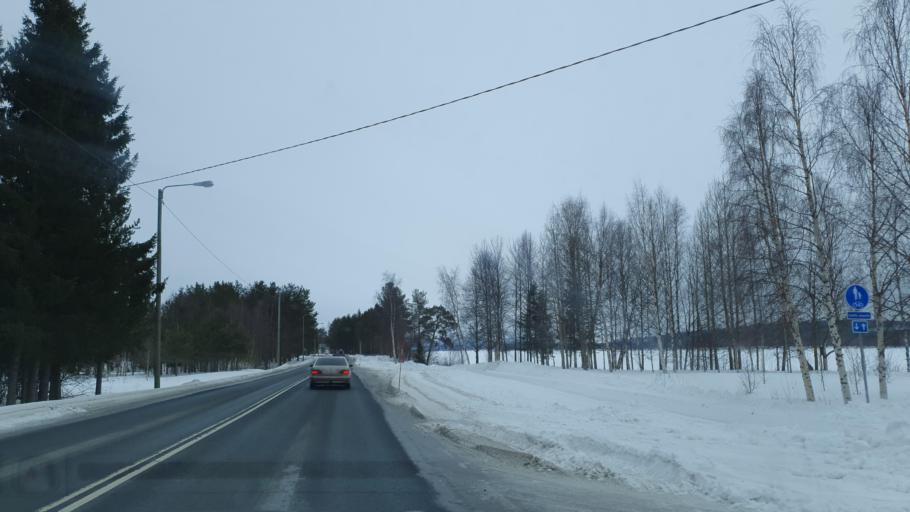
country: FI
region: Lapland
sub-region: Torniolaakso
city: Pello
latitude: 66.5930
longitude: 23.8868
